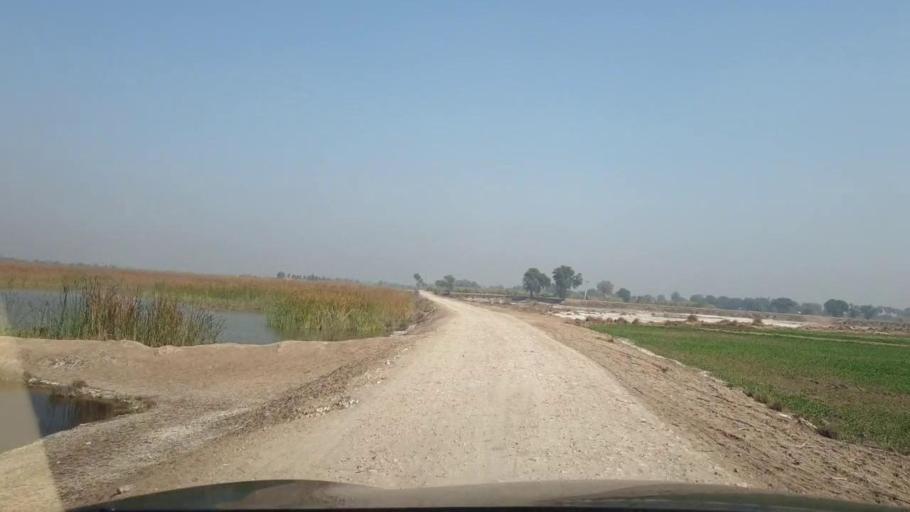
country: PK
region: Sindh
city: Ubauro
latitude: 28.1298
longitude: 69.7518
